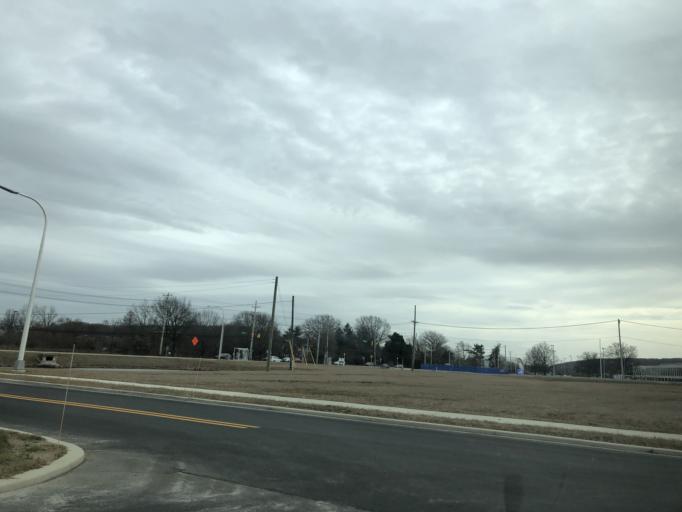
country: US
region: Delaware
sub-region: New Castle County
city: Newark
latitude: 39.6683
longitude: -75.7541
